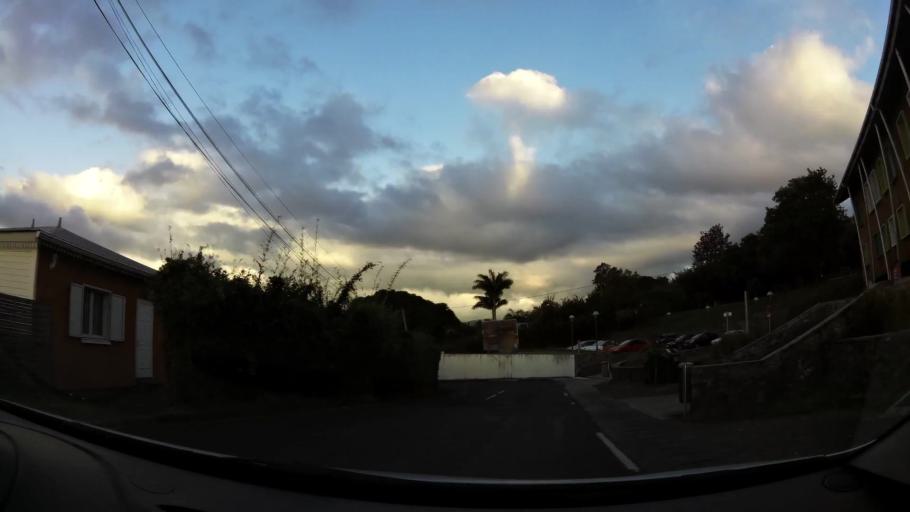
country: RE
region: Reunion
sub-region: Reunion
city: Saint-Denis
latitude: -20.9160
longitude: 55.4594
